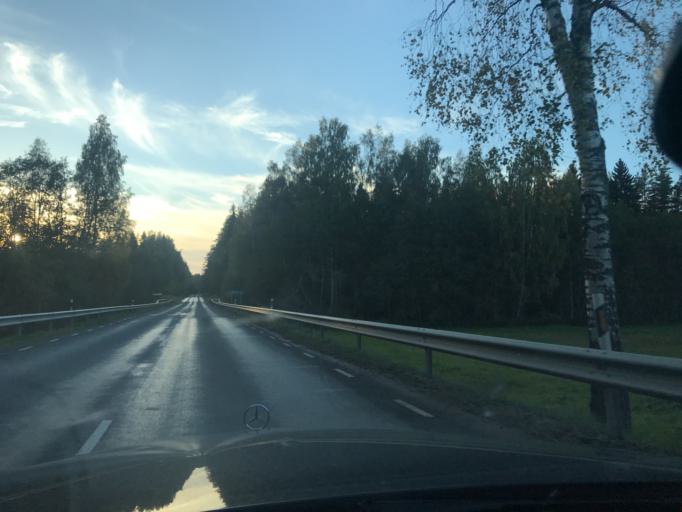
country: EE
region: Vorumaa
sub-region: Voru linn
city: Voru
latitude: 57.8784
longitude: 26.7816
